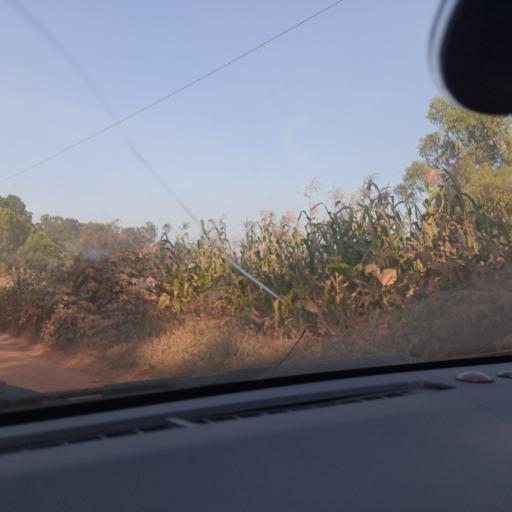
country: UG
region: Central Region
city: Masaka
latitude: -0.3315
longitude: 31.7354
